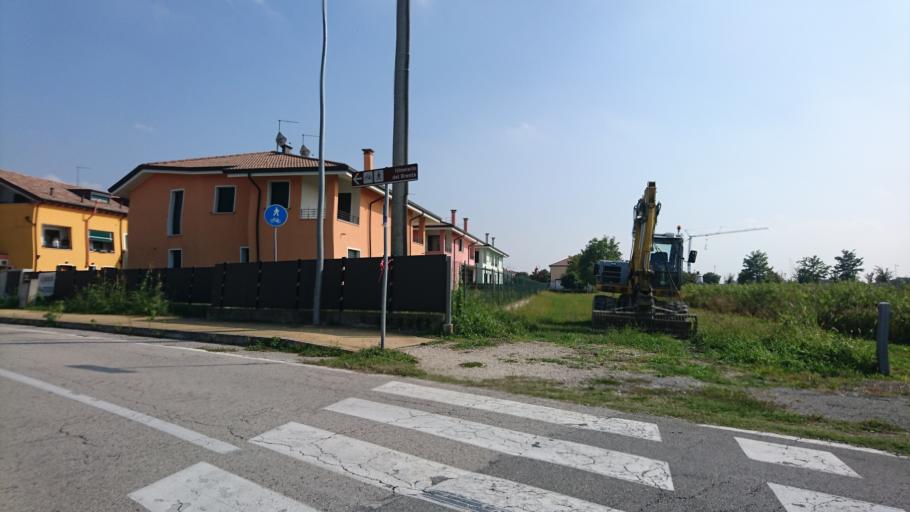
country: IT
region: Veneto
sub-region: Provincia di Padova
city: Tremignon
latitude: 45.5103
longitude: 11.8219
